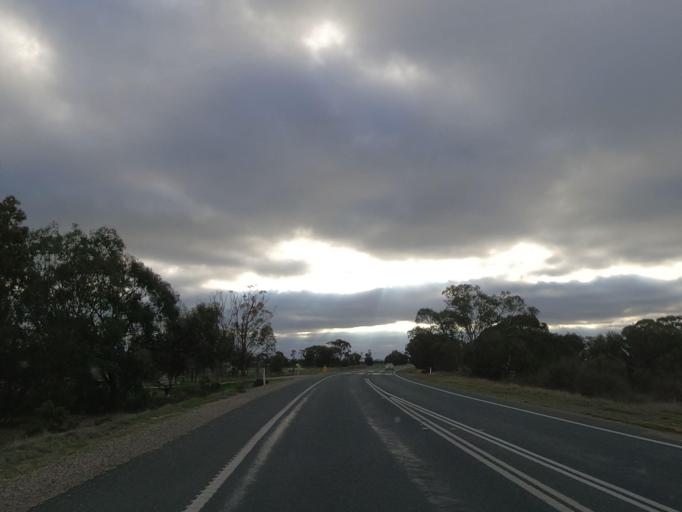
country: AU
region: Victoria
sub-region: Swan Hill
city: Swan Hill
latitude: -35.7325
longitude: 143.8970
